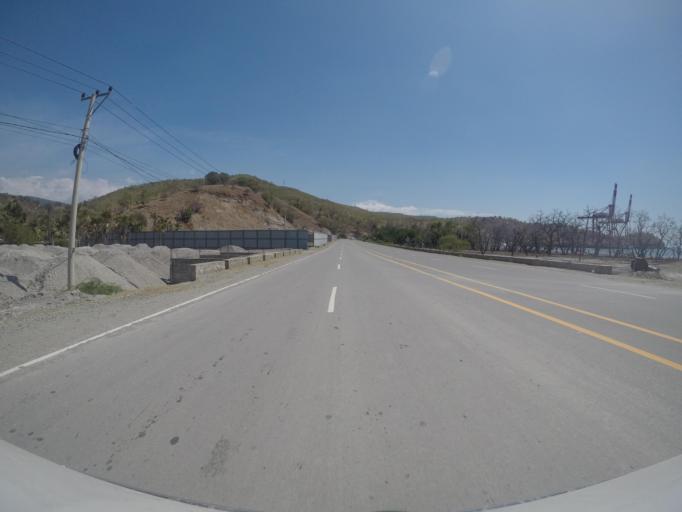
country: TL
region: Dili
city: Dili
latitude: -8.5733
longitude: 125.4830
